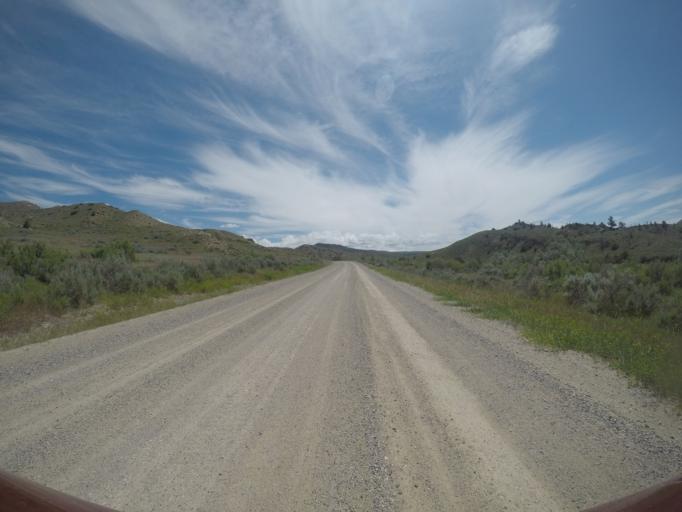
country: US
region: Montana
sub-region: Carbon County
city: Red Lodge
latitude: 45.2096
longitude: -108.8346
